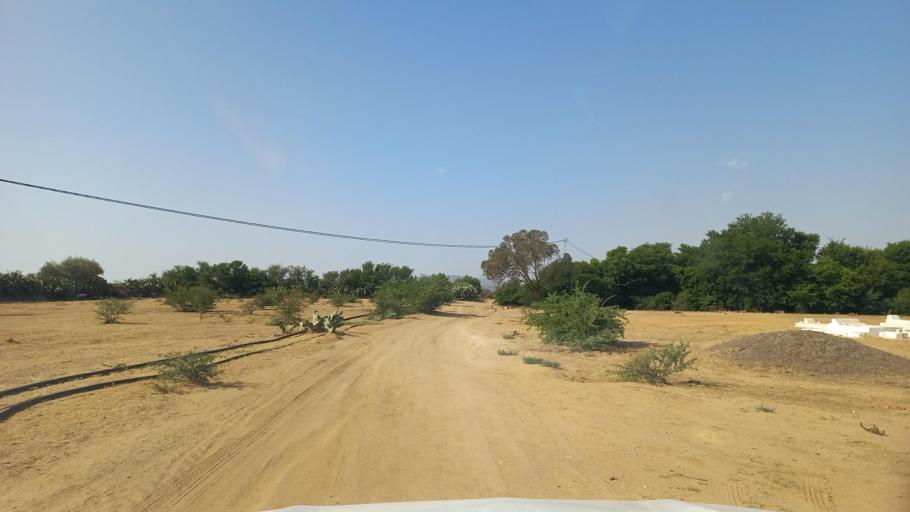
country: TN
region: Al Qasrayn
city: Kasserine
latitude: 35.2449
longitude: 9.0423
